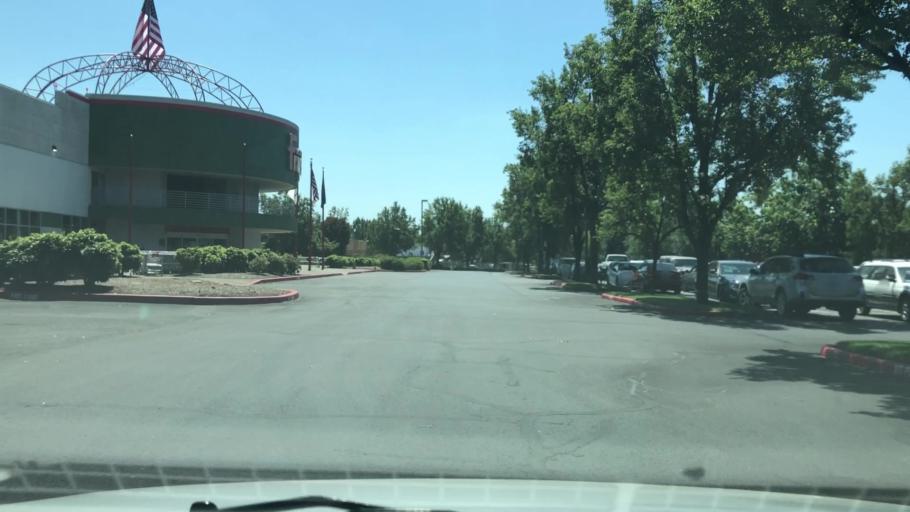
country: US
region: Oregon
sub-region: Clackamas County
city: Wilsonville
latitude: 45.3071
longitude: -122.7668
